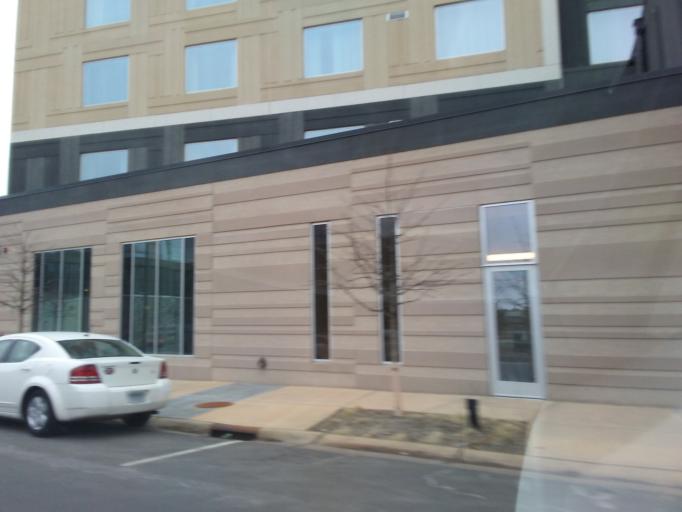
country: US
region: Minnesota
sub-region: Hennepin County
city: Richfield
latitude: 44.8575
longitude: -93.2255
